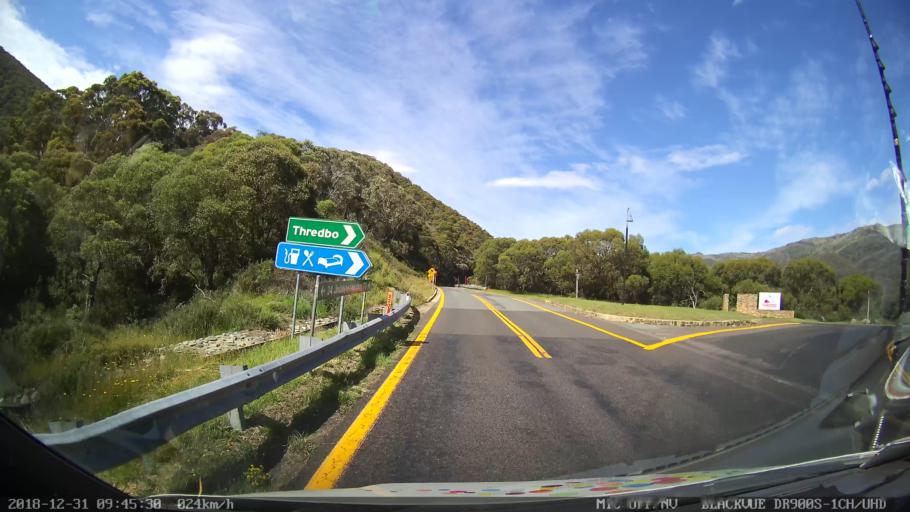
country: AU
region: New South Wales
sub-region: Snowy River
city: Jindabyne
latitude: -36.5000
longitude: 148.3169
